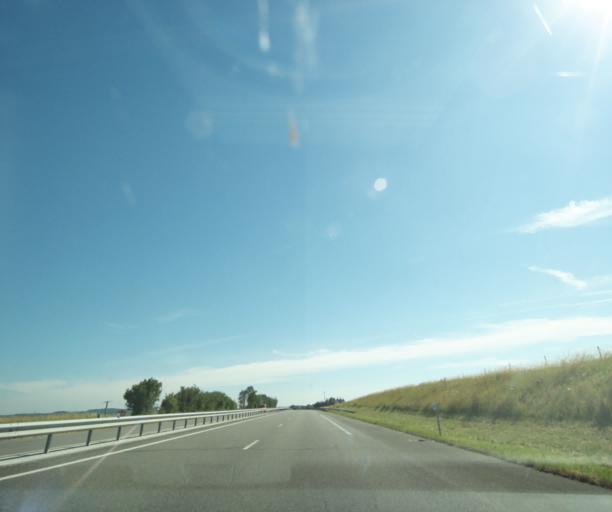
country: FR
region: Lorraine
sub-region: Departement des Vosges
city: Bulgneville
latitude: 48.1834
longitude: 5.7509
